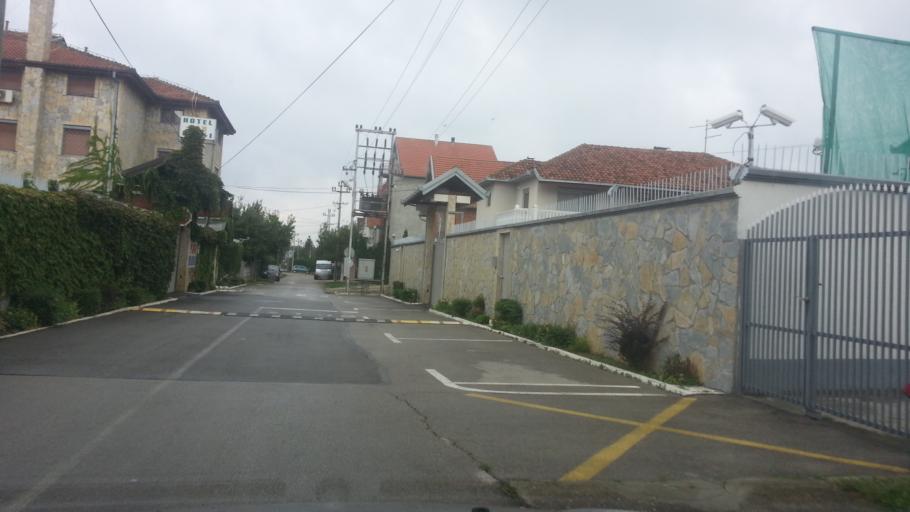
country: RS
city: Novi Banovci
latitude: 44.9443
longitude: 20.2875
